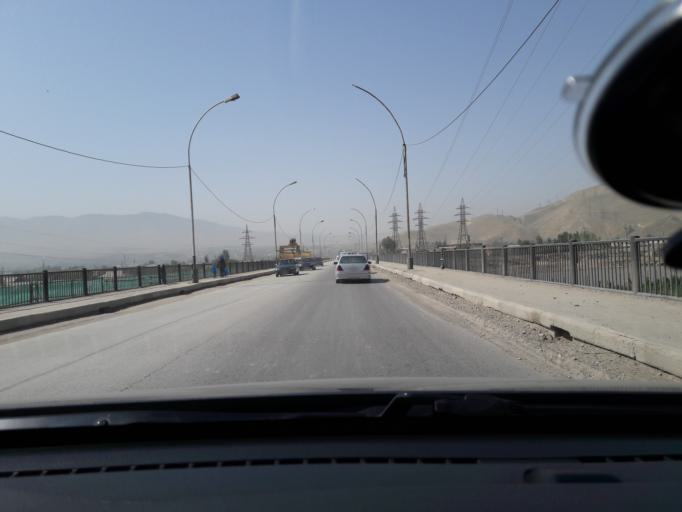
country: TJ
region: Dushanbe
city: Boshkengash
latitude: 38.4595
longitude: 68.7367
